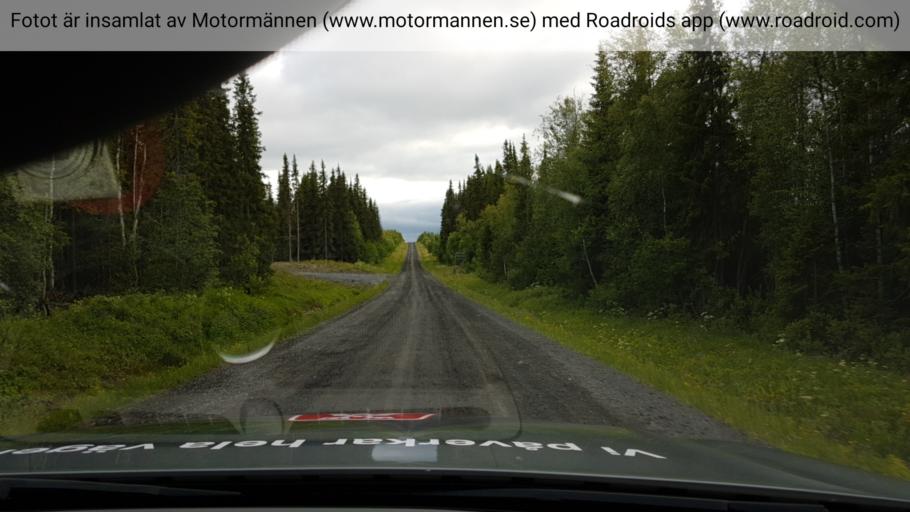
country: SE
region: Jaemtland
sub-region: OEstersunds Kommun
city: Lit
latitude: 63.6320
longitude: 15.0386
